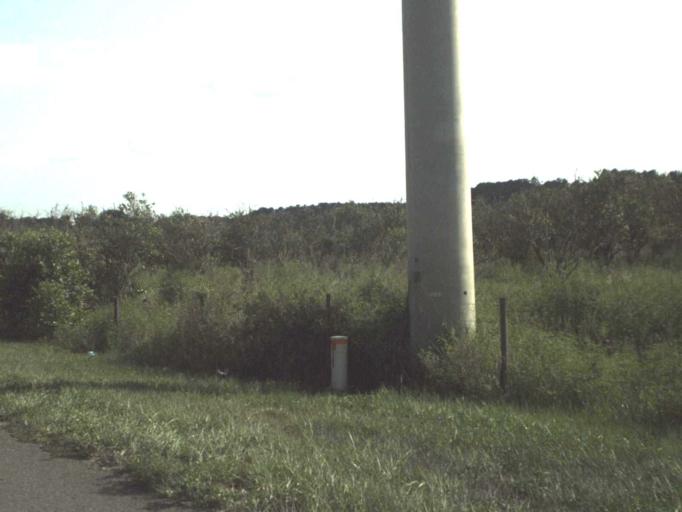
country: US
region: Florida
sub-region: Lake County
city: Groveland
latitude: 28.5478
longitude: -81.8516
